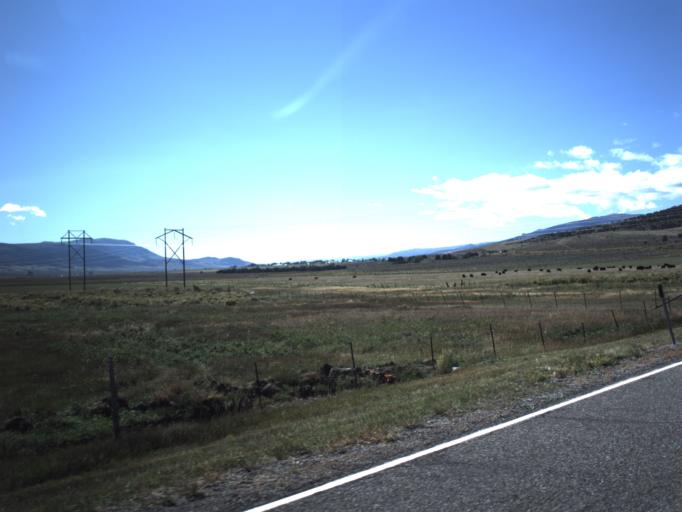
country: US
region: Utah
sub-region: Wayne County
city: Loa
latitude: 38.5581
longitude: -111.8605
